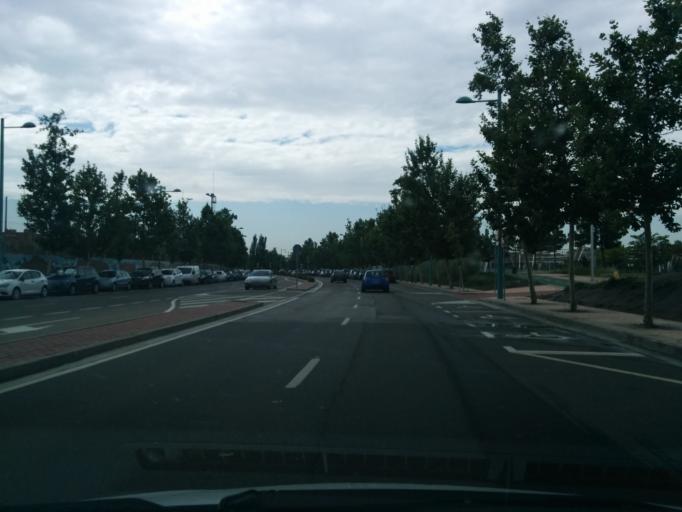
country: ES
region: Aragon
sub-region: Provincia de Zaragoza
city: Almozara
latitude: 41.6683
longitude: -0.8963
